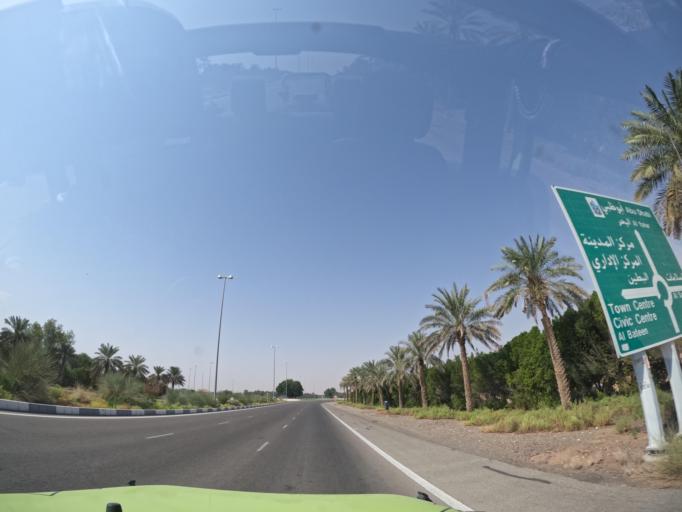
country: AE
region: Abu Dhabi
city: Al Ain
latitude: 24.2042
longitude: 55.5959
